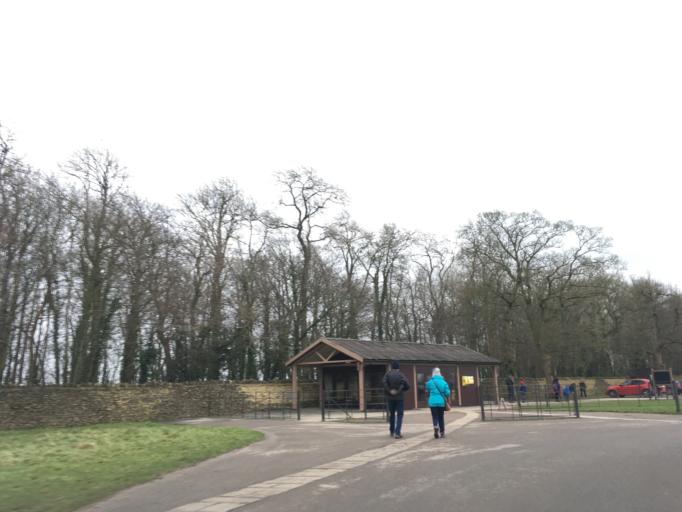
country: GB
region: England
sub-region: South Gloucestershire
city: Hinton
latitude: 51.4801
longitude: -2.3630
